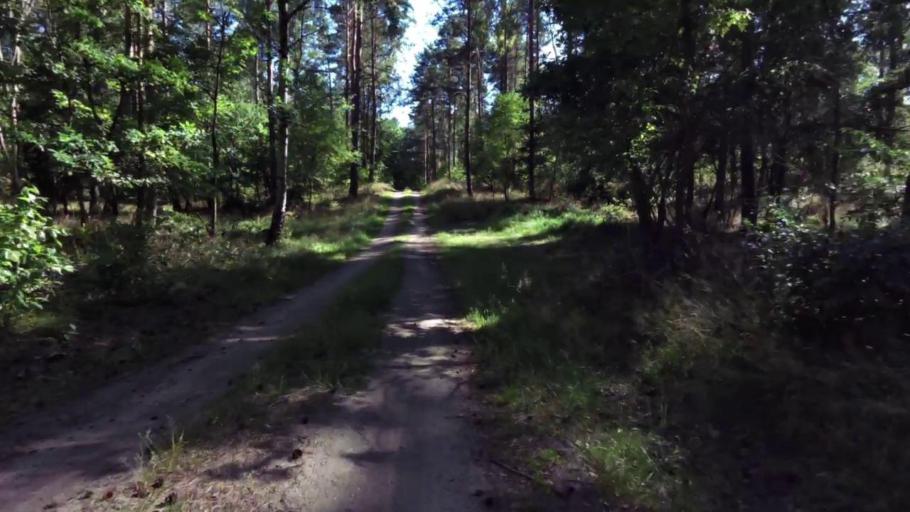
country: PL
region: West Pomeranian Voivodeship
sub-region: Powiat szczecinecki
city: Borne Sulinowo
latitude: 53.6020
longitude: 16.6072
